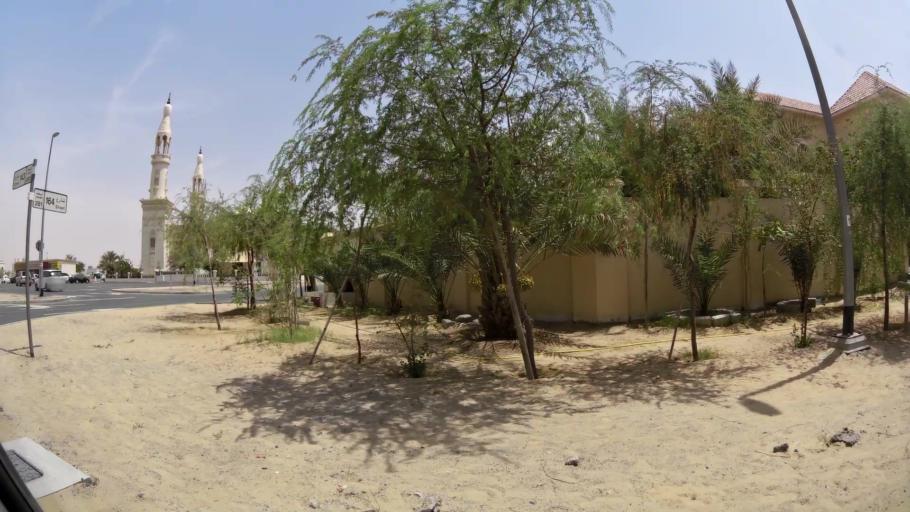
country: AE
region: Ash Shariqah
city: Sharjah
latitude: 25.2454
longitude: 55.5021
